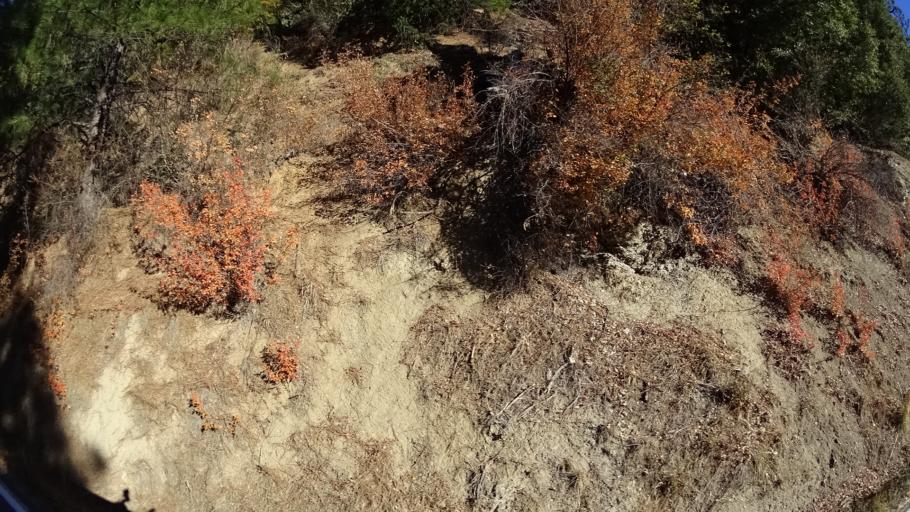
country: US
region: California
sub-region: Trinity County
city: Weaverville
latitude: 41.2105
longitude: -123.0449
